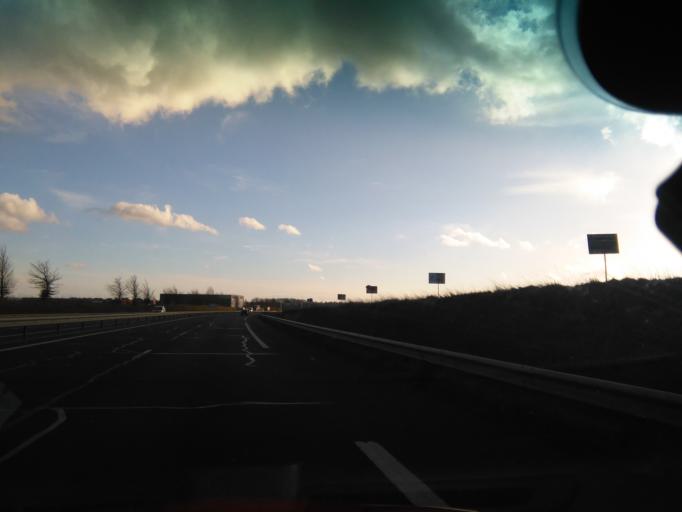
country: FR
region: Lower Normandy
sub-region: Departement du Calvados
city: Falaise
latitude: 48.9184
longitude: -0.2058
